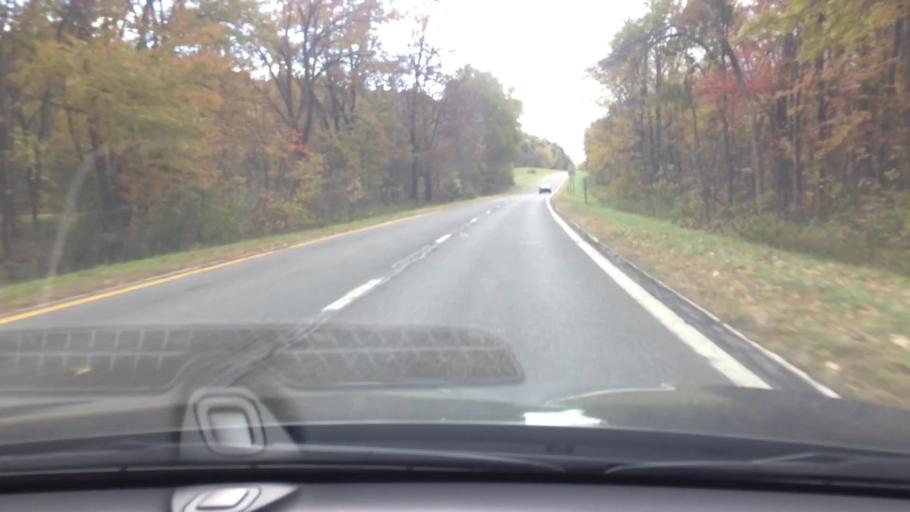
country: US
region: New York
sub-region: Dutchess County
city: Pine Plains
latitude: 41.9477
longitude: -73.7525
